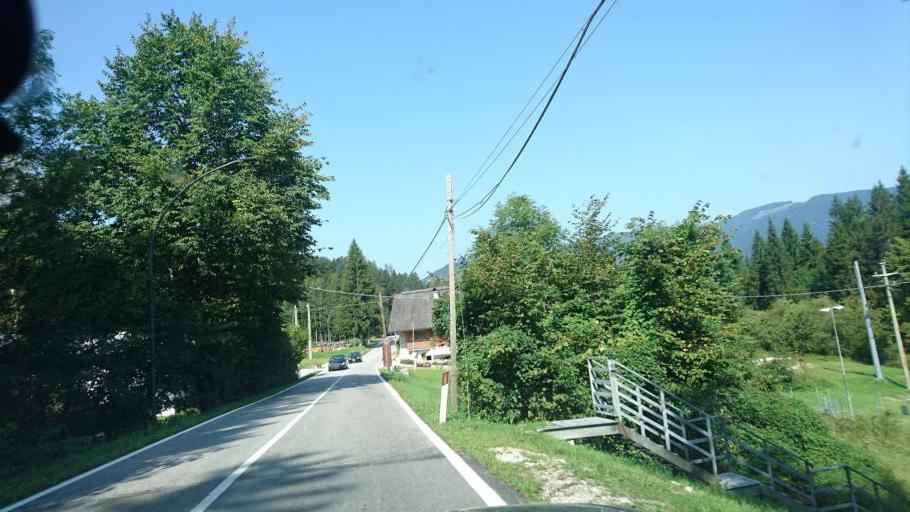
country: IT
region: Friuli Venezia Giulia
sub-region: Provincia di Udine
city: Tarvisio
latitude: 46.4966
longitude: 13.6355
